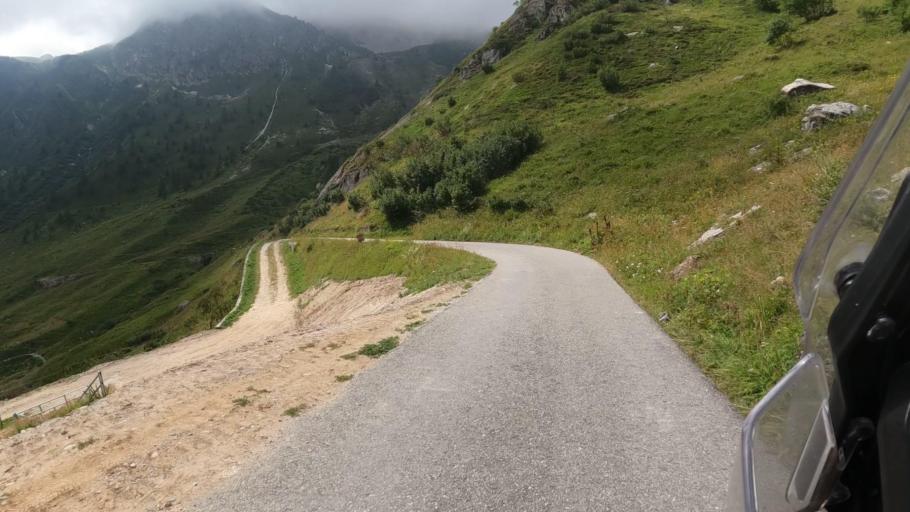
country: IT
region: Piedmont
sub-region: Provincia di Cuneo
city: Campomolino
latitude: 44.3920
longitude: 7.1486
